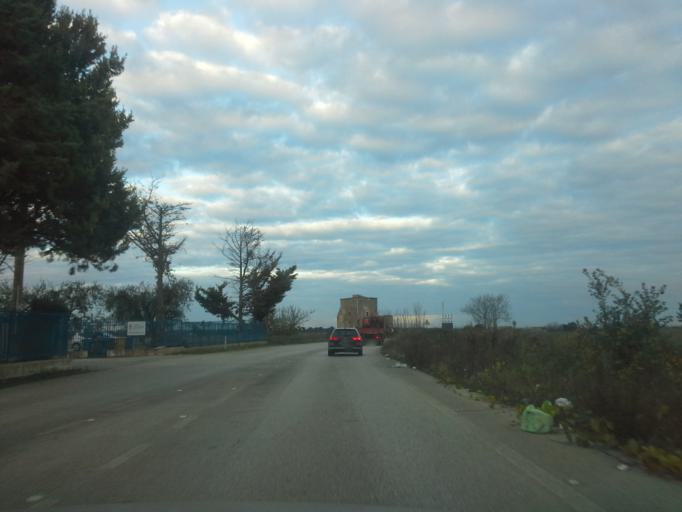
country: IT
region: Apulia
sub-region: Provincia di Bari
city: Adelfia
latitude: 41.0062
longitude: 16.8580
